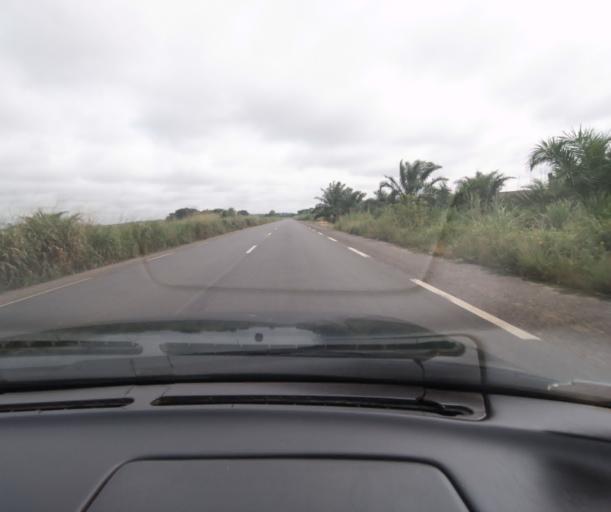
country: CM
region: Centre
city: Saa
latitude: 4.3822
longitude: 11.2561
